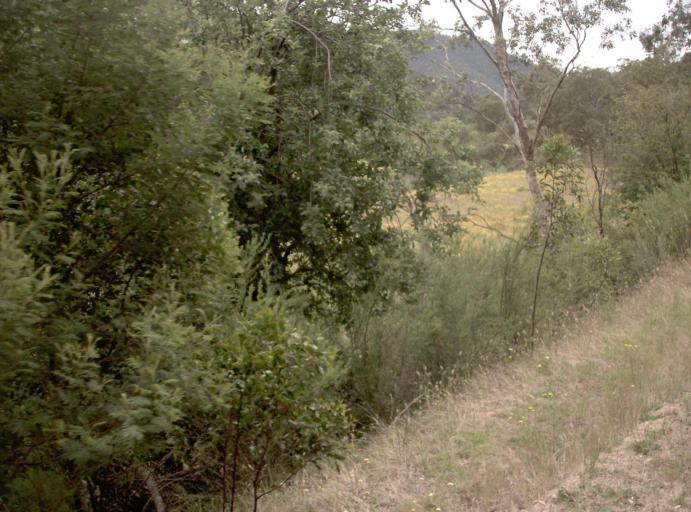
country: AU
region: Victoria
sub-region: East Gippsland
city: Bairnsdale
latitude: -37.5331
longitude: 147.2169
